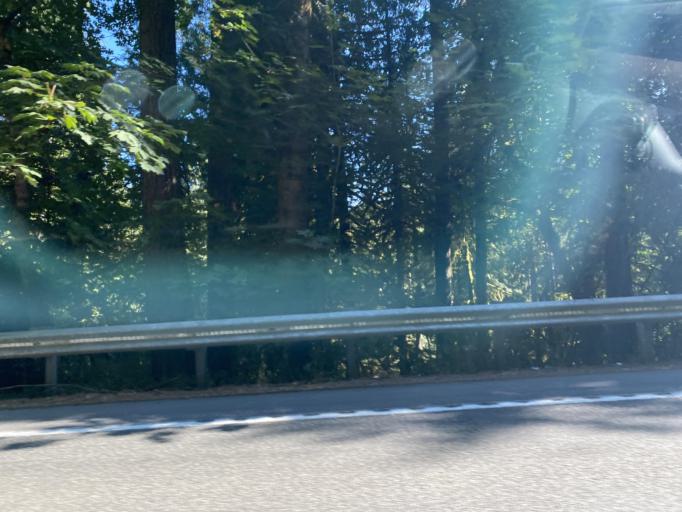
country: US
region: Washington
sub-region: Thurston County
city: Rainier
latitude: 46.9355
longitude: -122.7608
